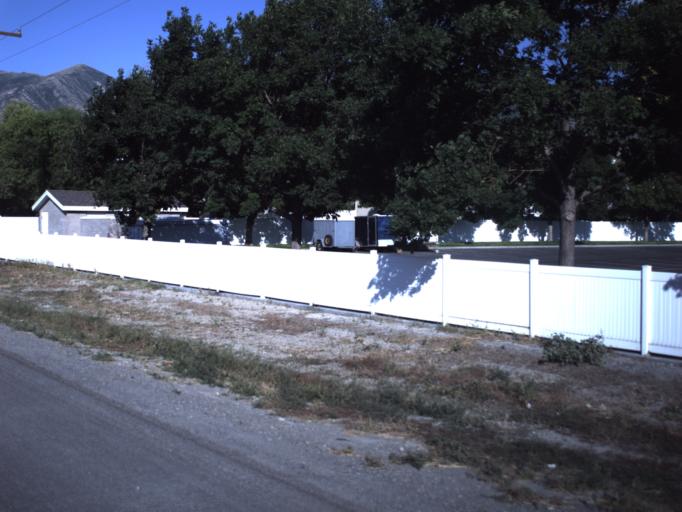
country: US
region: Utah
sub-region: Tooele County
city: Stansbury park
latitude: 40.6515
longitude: -112.2952
